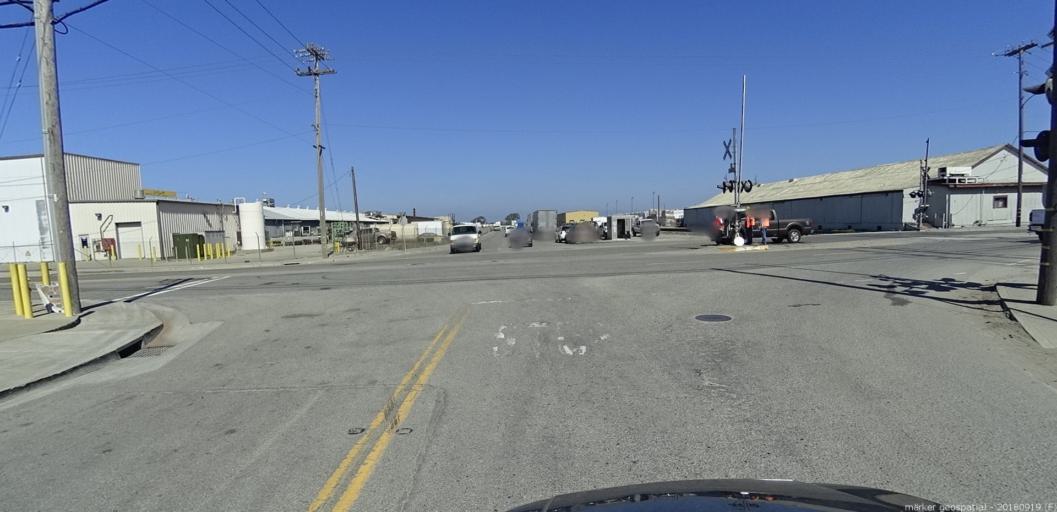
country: US
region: California
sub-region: Monterey County
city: Castroville
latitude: 36.7577
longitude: -121.7440
